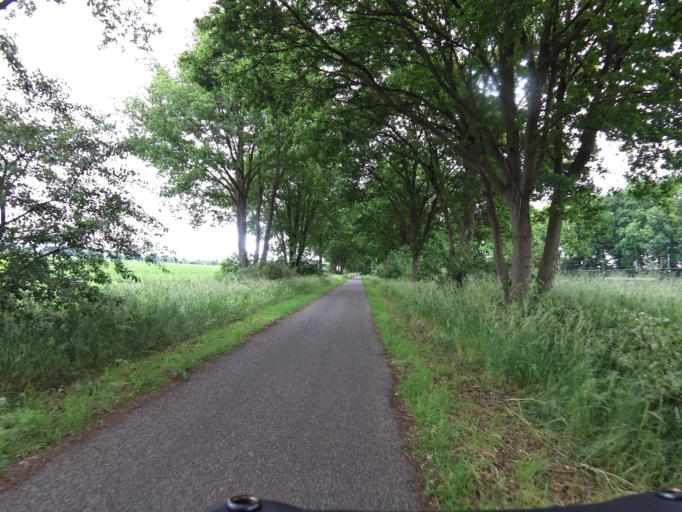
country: NL
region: North Brabant
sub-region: Gemeente Baarle-Nassau
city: Baarle-Nassau
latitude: 51.4681
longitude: 4.9464
